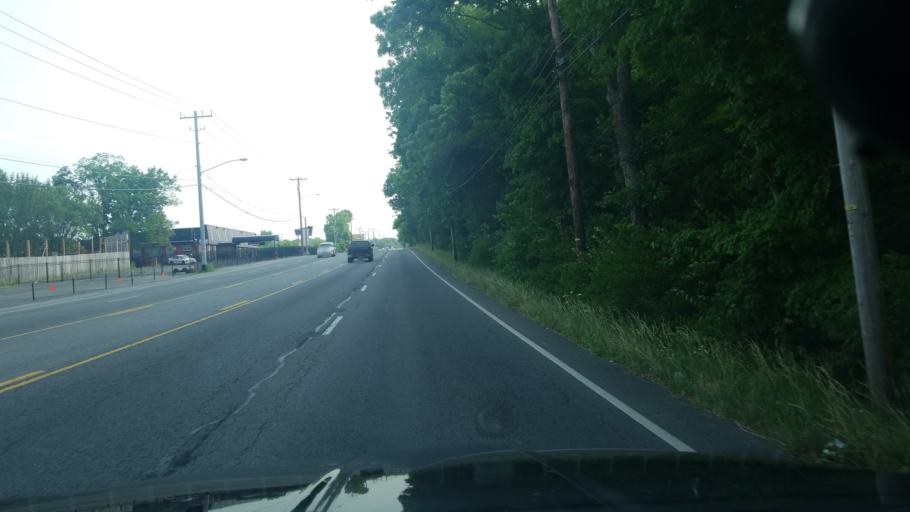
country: US
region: Tennessee
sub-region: Davidson County
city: Goodlettsville
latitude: 36.2733
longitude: -86.7535
